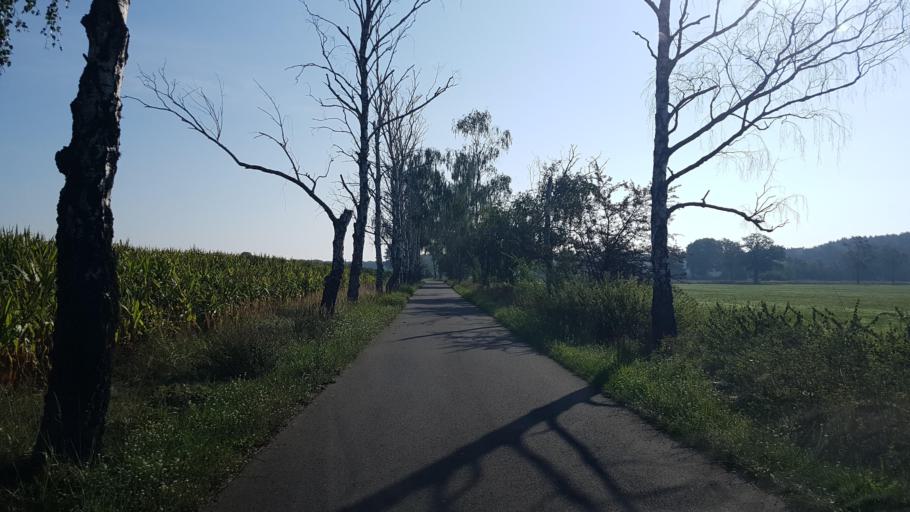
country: DE
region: Brandenburg
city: Brandenburg an der Havel
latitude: 52.4583
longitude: 12.5876
